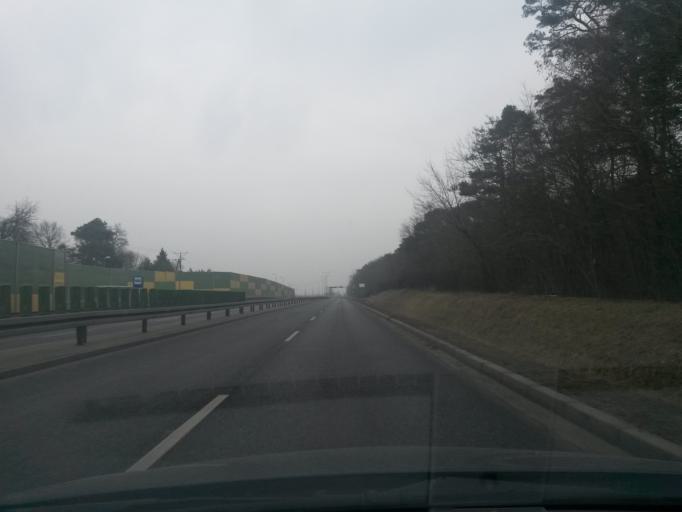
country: PL
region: Masovian Voivodeship
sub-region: Powiat legionowski
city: Serock
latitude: 52.4885
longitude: 21.0461
